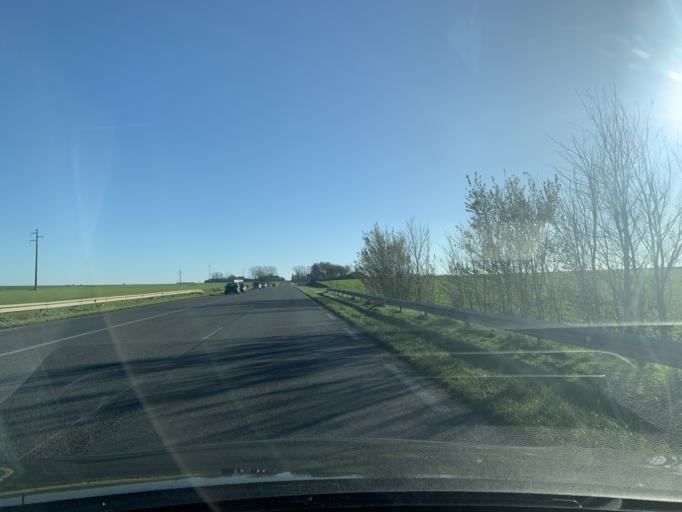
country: FR
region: Nord-Pas-de-Calais
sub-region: Departement du Nord
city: Escaudoeuvres
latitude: 50.1582
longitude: 3.3065
